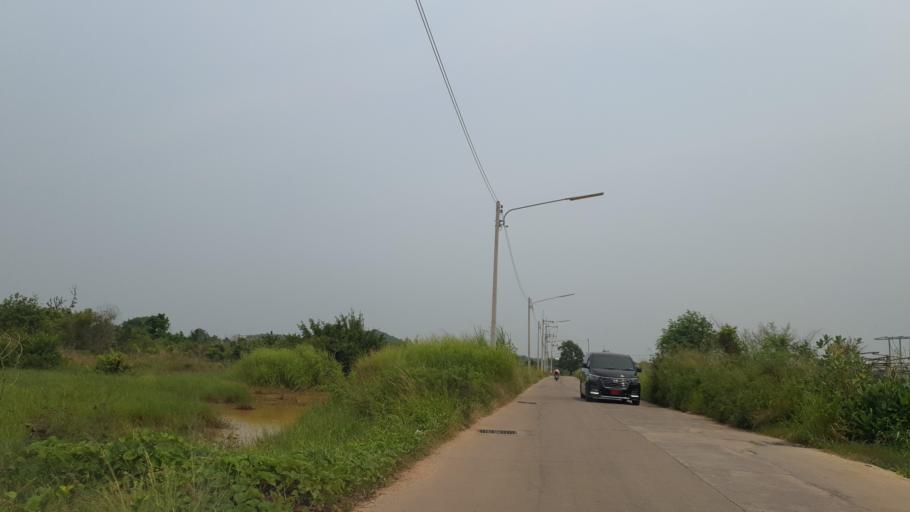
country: TH
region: Chon Buri
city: Phatthaya
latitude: 12.8890
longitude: 100.9273
